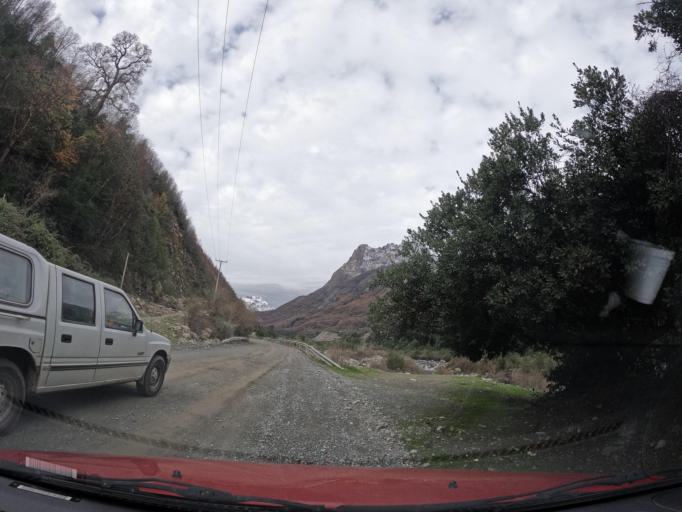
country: CL
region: Maule
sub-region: Provincia de Linares
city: Colbun
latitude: -35.8596
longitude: -71.2206
